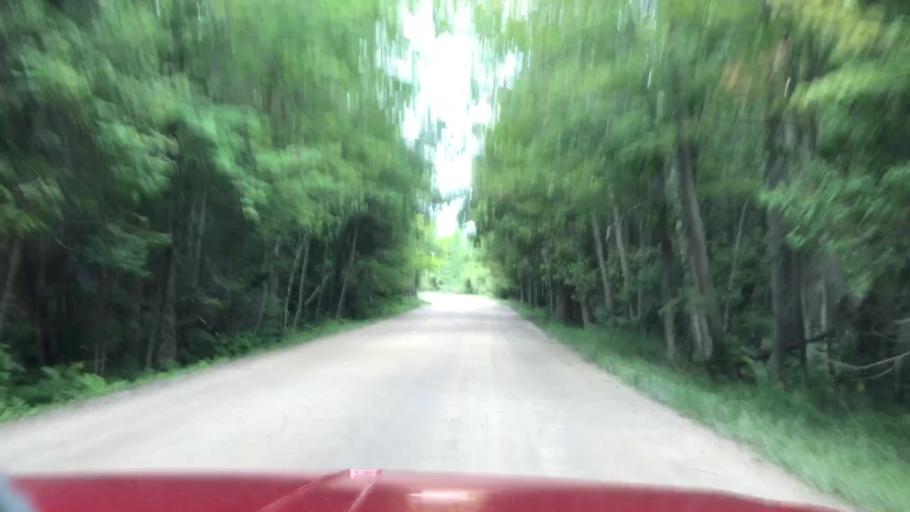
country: US
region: Michigan
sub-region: Charlevoix County
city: Charlevoix
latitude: 45.7287
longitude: -85.5402
